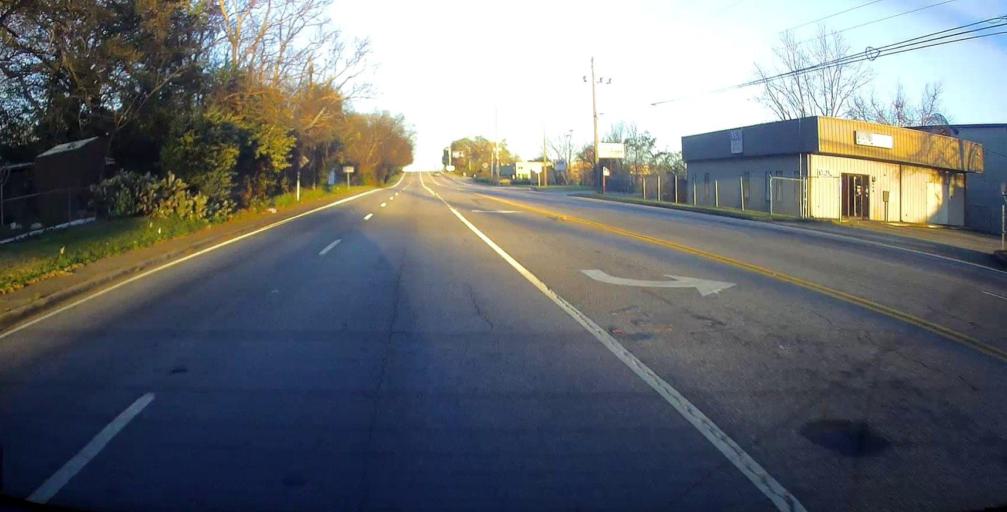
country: US
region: Alabama
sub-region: Russell County
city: Phenix City
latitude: 32.5072
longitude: -84.9886
